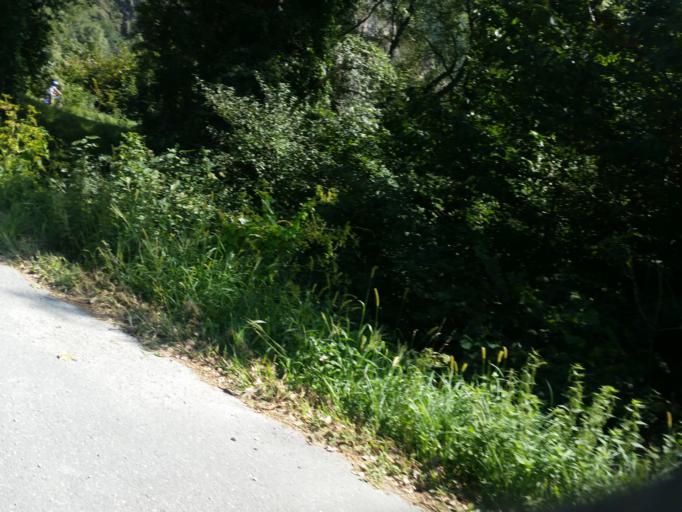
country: CH
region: Valais
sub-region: Saint-Maurice District
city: Vernayaz
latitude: 46.1421
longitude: 7.0446
